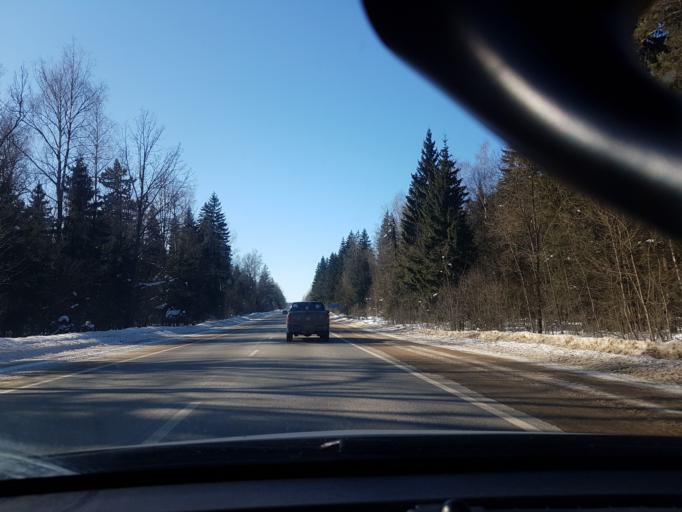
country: RU
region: Moskovskaya
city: Kostrovo
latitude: 55.9138
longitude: 36.7034
